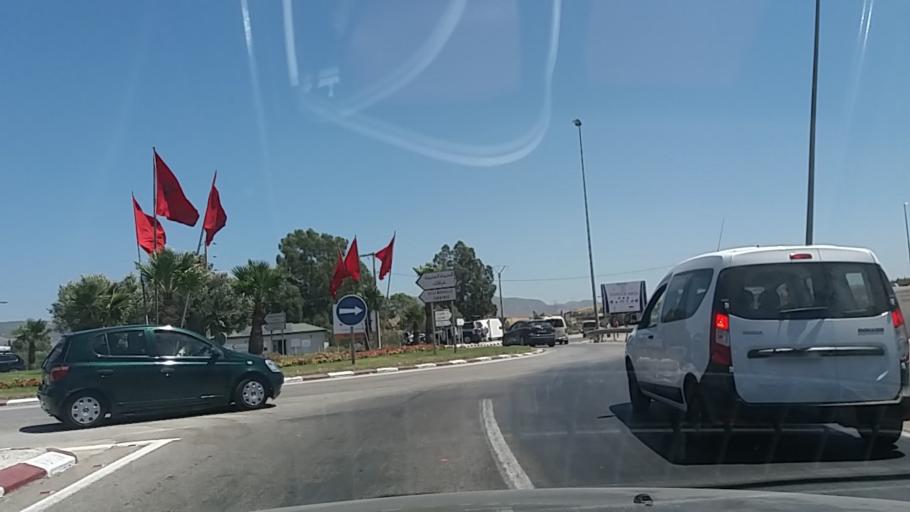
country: MA
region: Tanger-Tetouan
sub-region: Tanger-Assilah
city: Tangier
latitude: 35.6775
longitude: -5.7053
